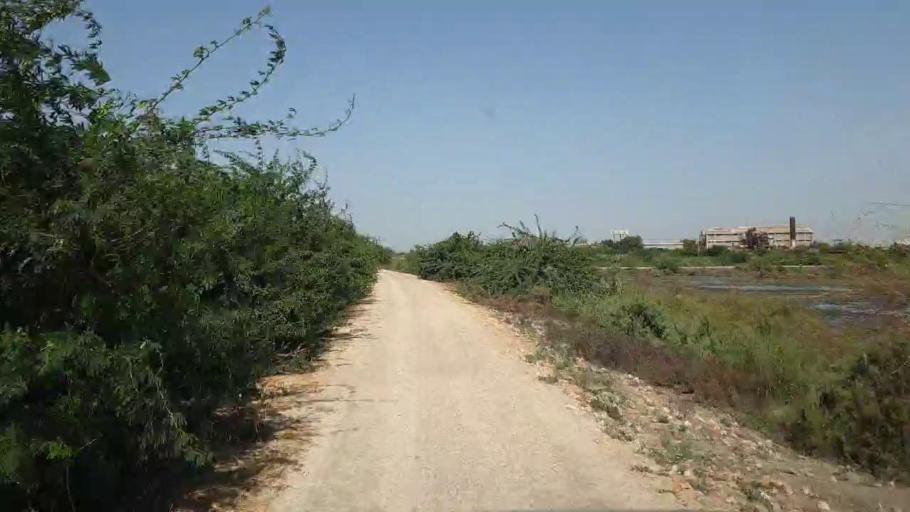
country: PK
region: Sindh
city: Tando Bago
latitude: 24.7394
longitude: 69.0743
